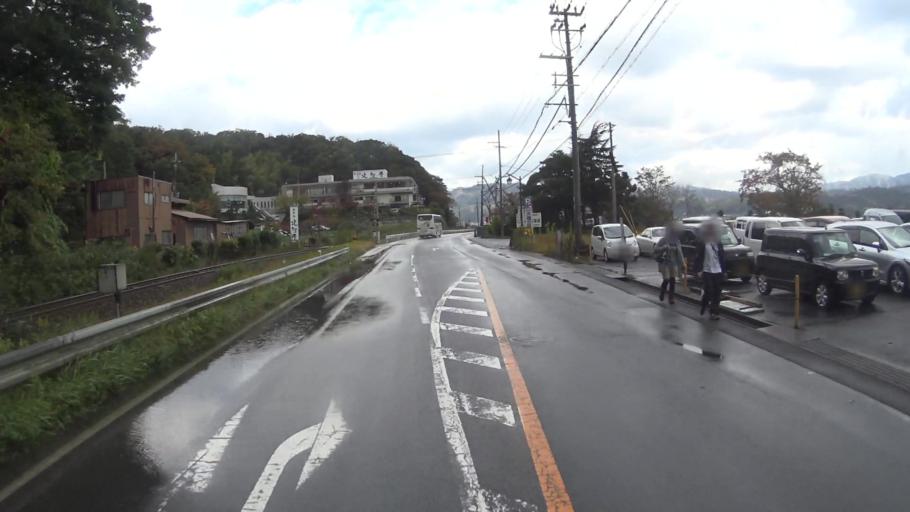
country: JP
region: Kyoto
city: Miyazu
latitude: 35.5590
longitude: 135.1788
